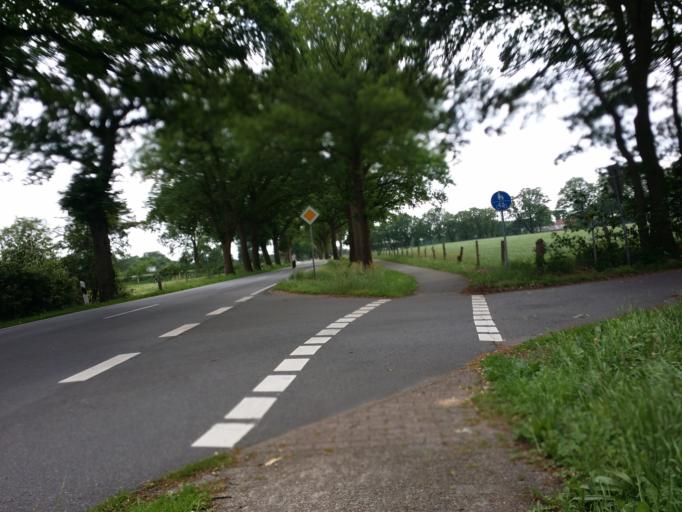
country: DE
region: Lower Saxony
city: Wiefelstede
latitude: 53.2733
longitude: 8.1108
